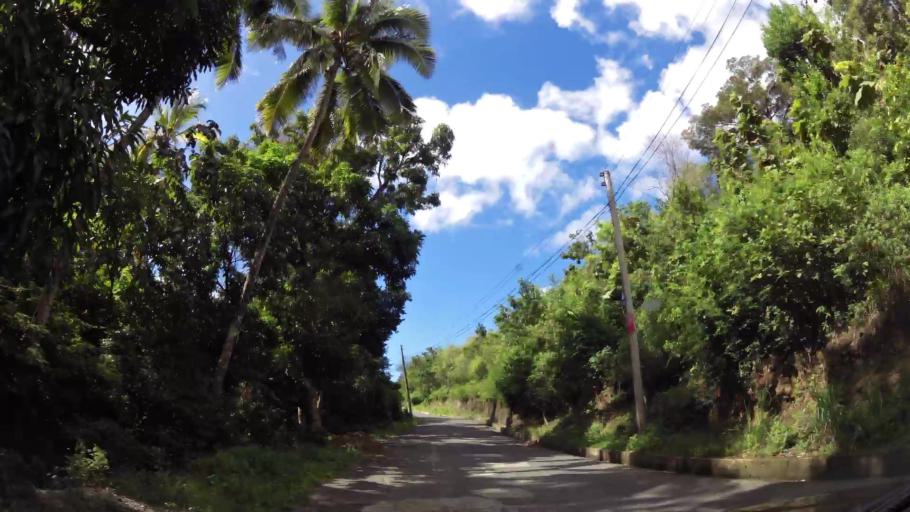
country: DM
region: Saint John
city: Portsmouth
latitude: 15.6061
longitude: -61.4622
